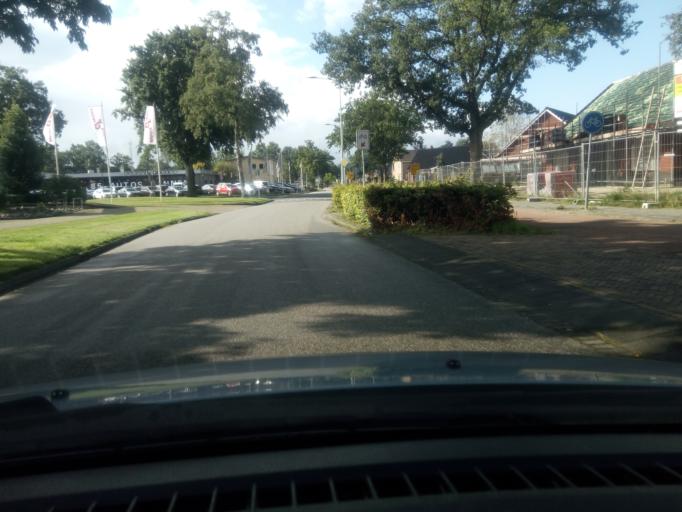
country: NL
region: Friesland
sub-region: Gemeente Achtkarspelen
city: Surhuisterveen
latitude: 53.1807
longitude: 6.1777
